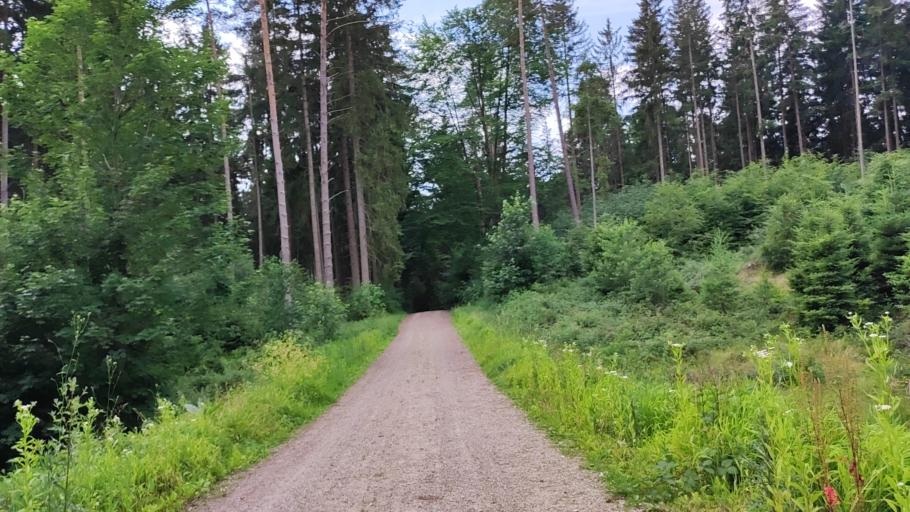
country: DE
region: Bavaria
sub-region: Swabia
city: Adelsried
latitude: 48.4111
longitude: 10.7096
